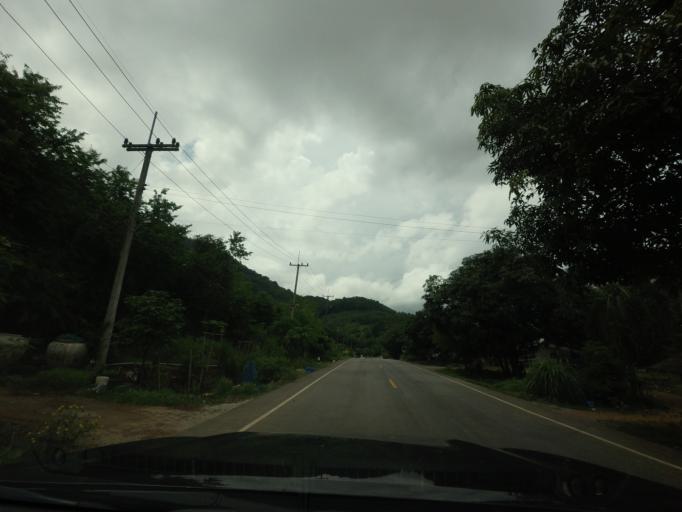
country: TH
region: Loei
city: Pak Chom
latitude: 18.0623
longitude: 101.7945
